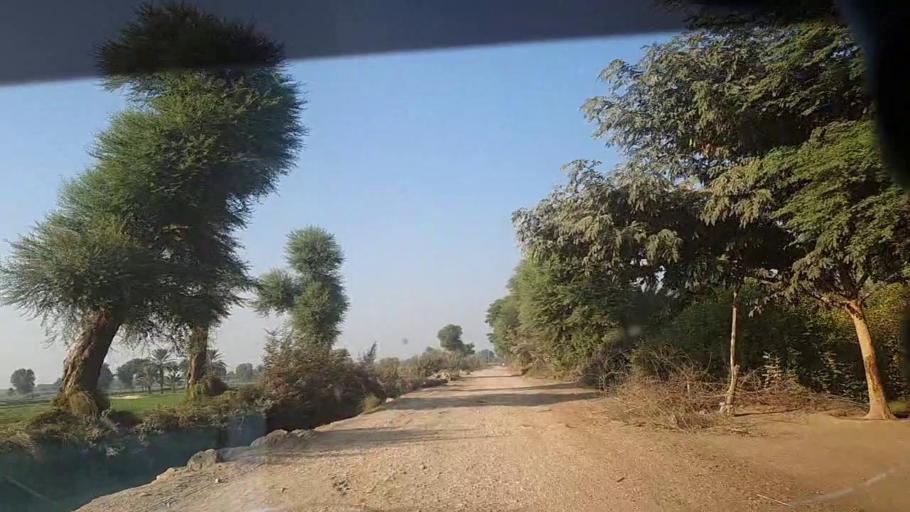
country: PK
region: Sindh
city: Sobhadero
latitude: 27.2601
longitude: 68.3507
